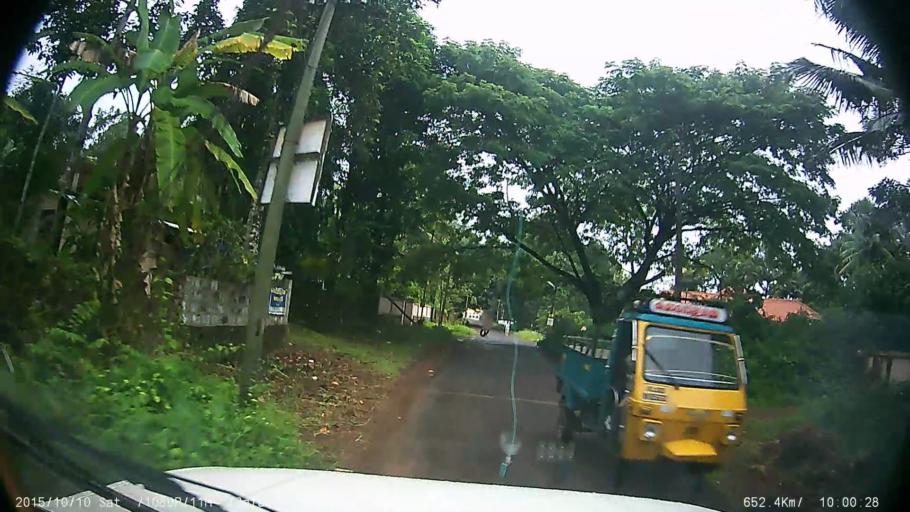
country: IN
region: Kerala
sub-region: Kottayam
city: Kottayam
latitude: 9.6411
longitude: 76.5355
